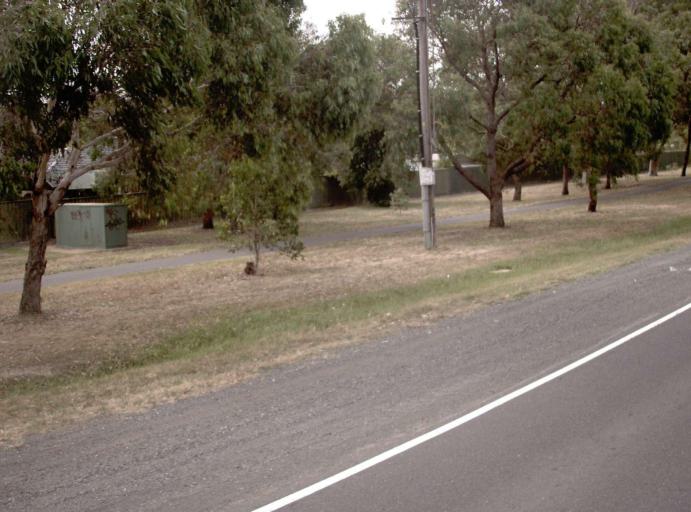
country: AU
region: Victoria
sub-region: Knox
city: Wantirna
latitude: -37.8624
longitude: 145.2386
